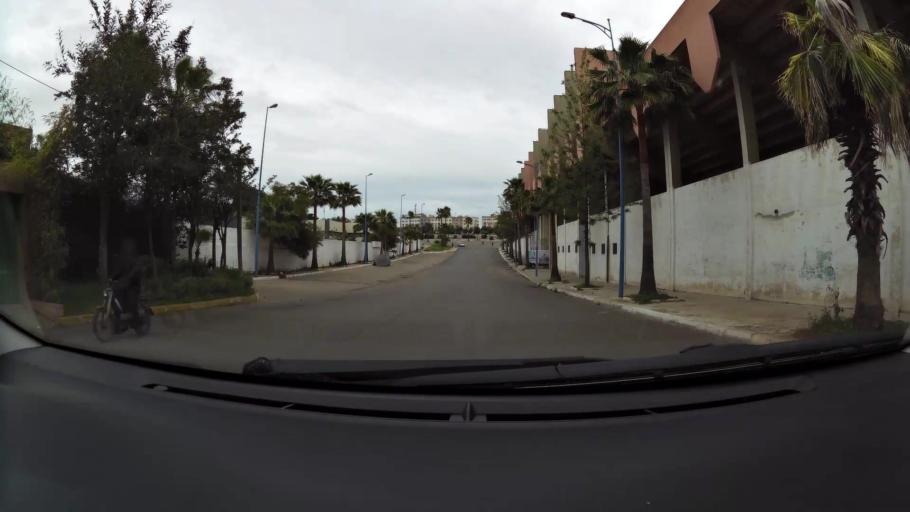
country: MA
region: Grand Casablanca
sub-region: Mediouna
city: Tit Mellil
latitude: 33.5652
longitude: -7.5371
